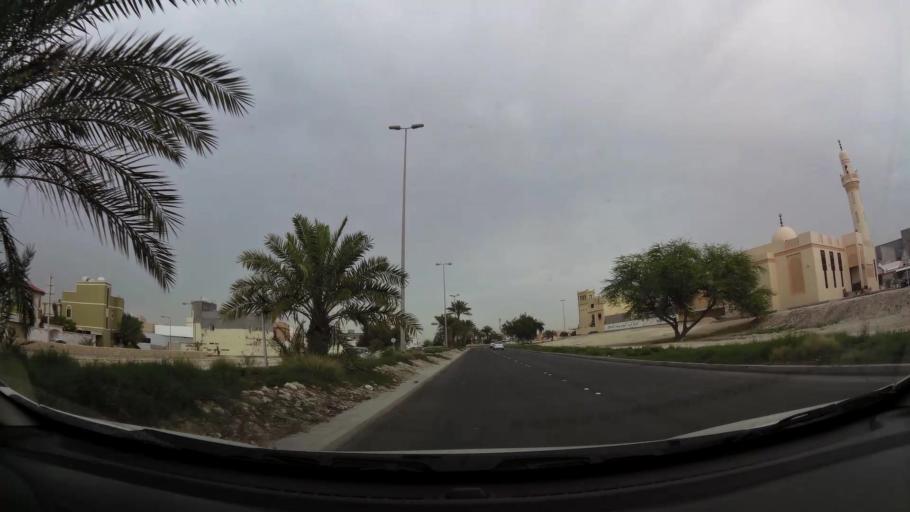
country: BH
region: Central Governorate
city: Dar Kulayb
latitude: 26.0669
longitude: 50.5078
